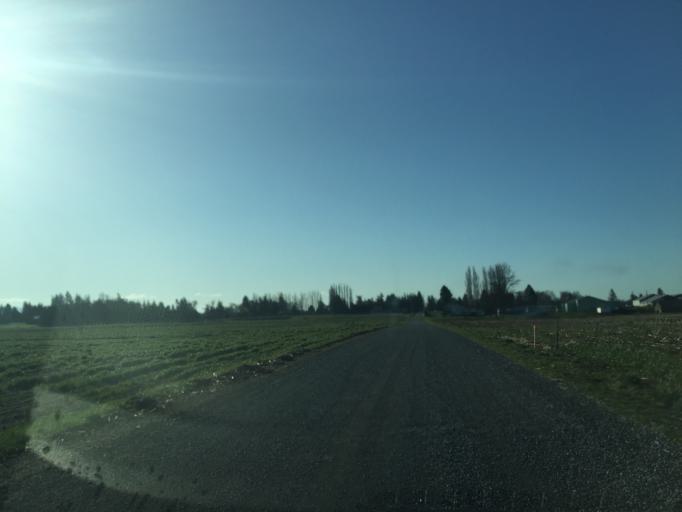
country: US
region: Washington
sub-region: Whatcom County
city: Lynden
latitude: 48.9168
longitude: -122.4642
